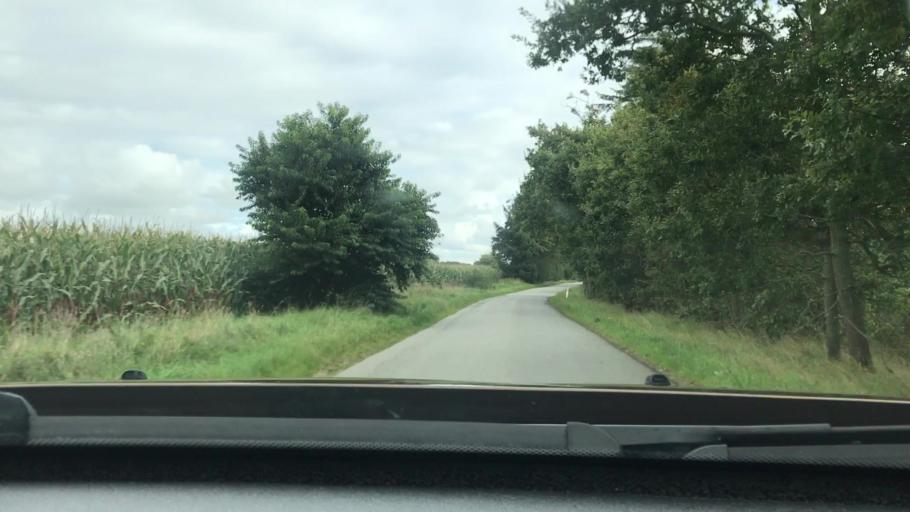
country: DK
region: South Denmark
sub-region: Esbjerg Kommune
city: Ribe
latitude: 55.3000
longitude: 8.7245
